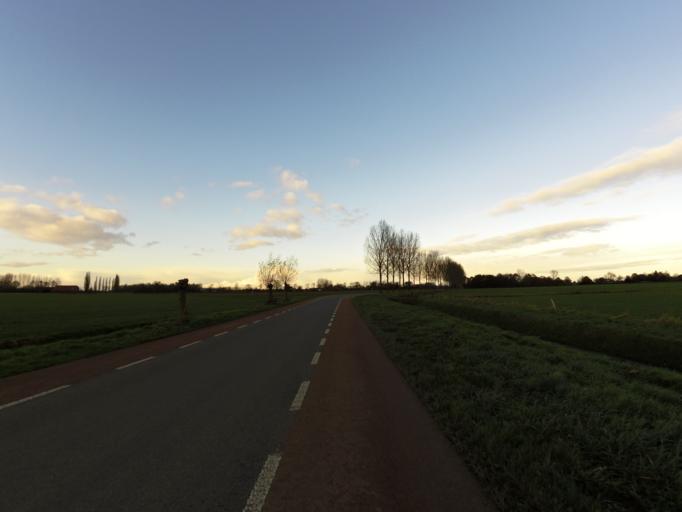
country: NL
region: Gelderland
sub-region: Oude IJsselstreek
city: Gendringen
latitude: 51.8656
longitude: 6.3476
